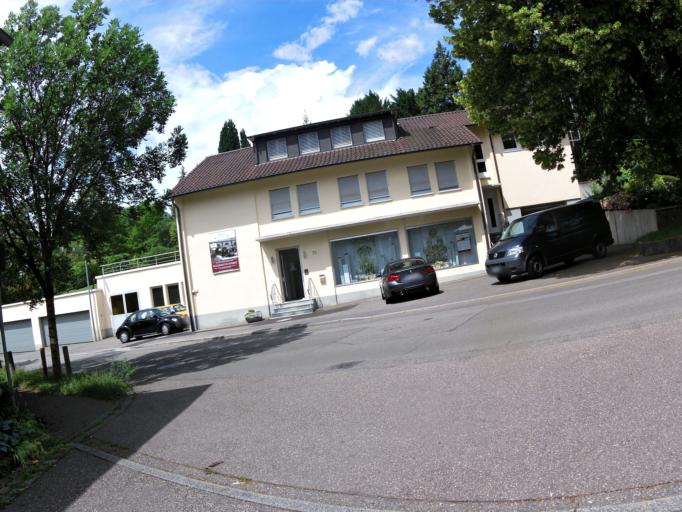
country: DE
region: Baden-Wuerttemberg
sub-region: Freiburg Region
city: Lahr
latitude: 48.3449
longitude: 7.8679
